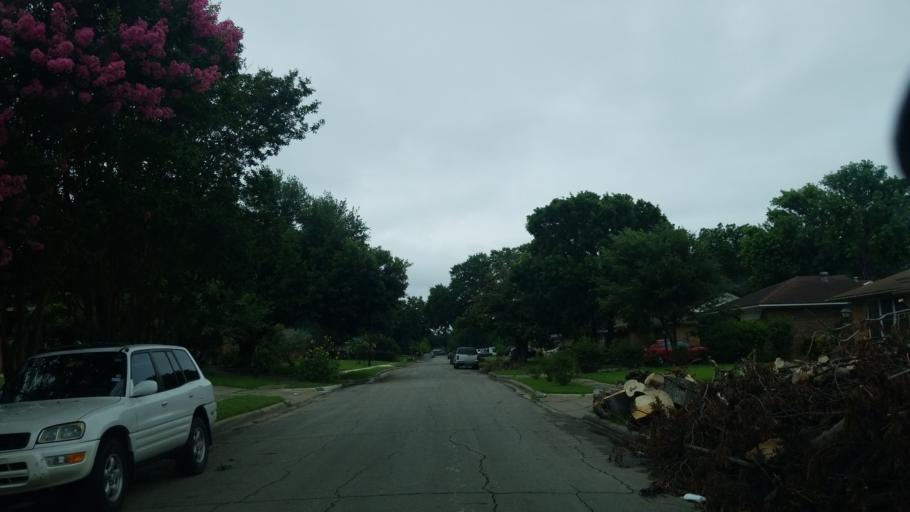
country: US
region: Texas
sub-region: Dallas County
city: Farmers Branch
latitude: 32.8927
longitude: -96.8797
